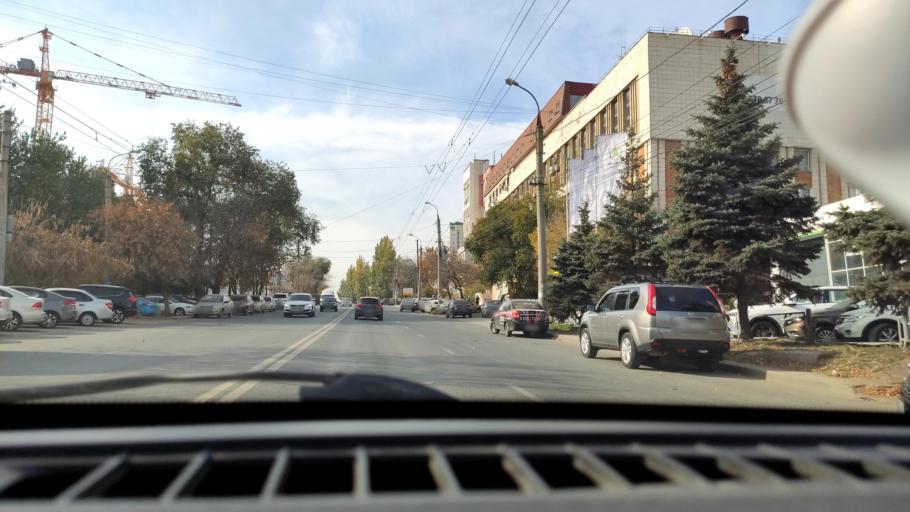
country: RU
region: Samara
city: Samara
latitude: 53.2127
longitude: 50.2187
